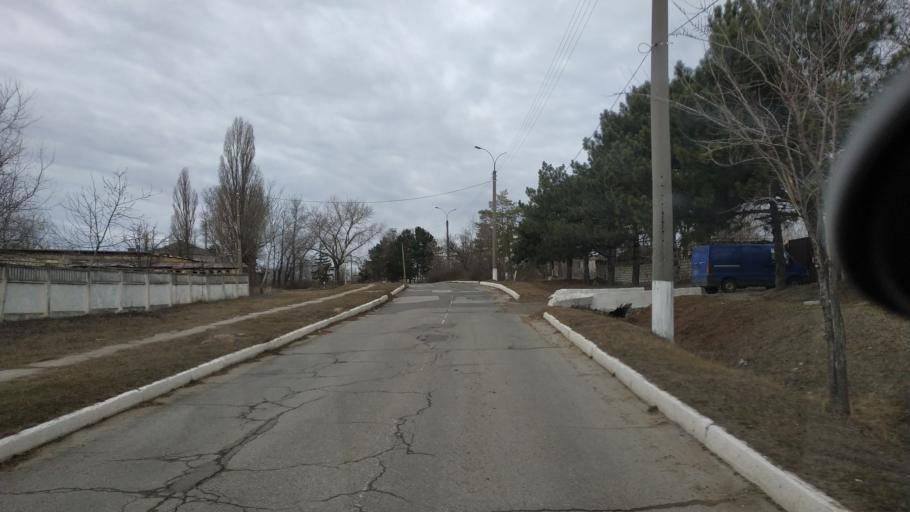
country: MD
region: Criuleni
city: Criuleni
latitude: 47.2198
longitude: 29.1568
